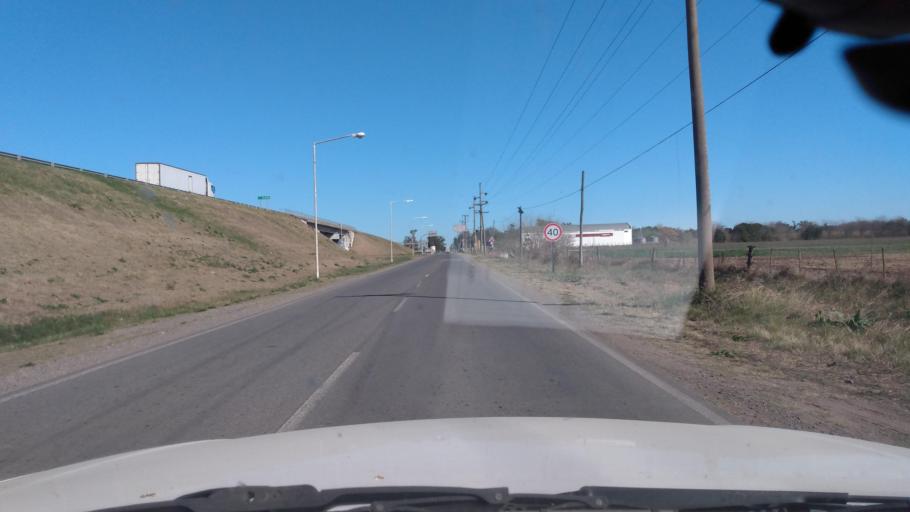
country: AR
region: Buenos Aires
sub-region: Partido de Mercedes
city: Mercedes
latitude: -34.6607
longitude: -59.3807
